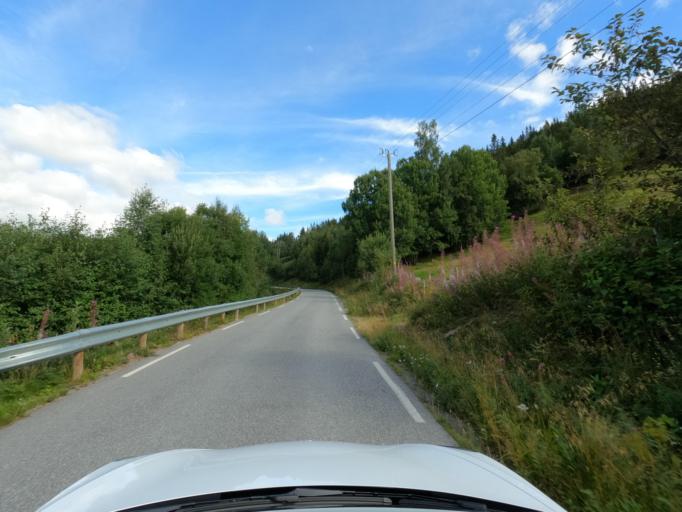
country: NO
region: Telemark
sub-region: Tinn
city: Rjukan
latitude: 60.0435
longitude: 8.7356
